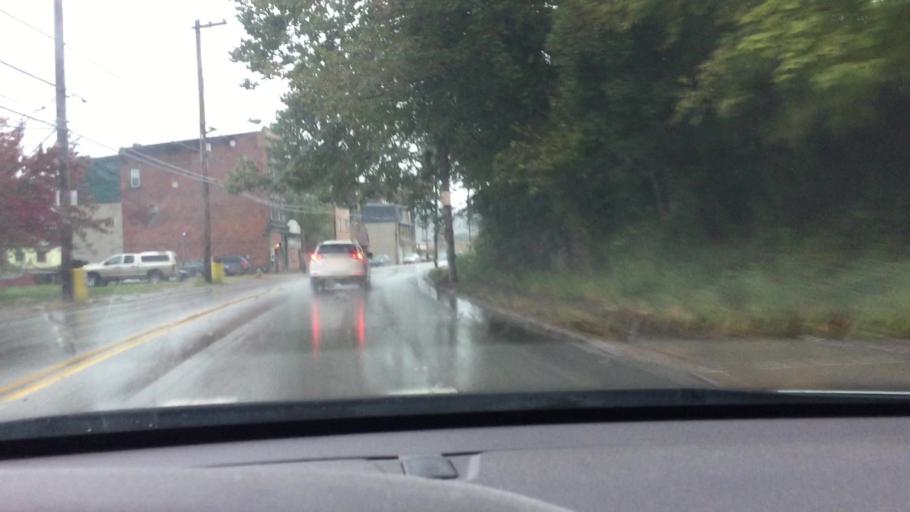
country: US
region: Pennsylvania
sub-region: Allegheny County
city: Homestead
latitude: 40.4018
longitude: -79.9406
